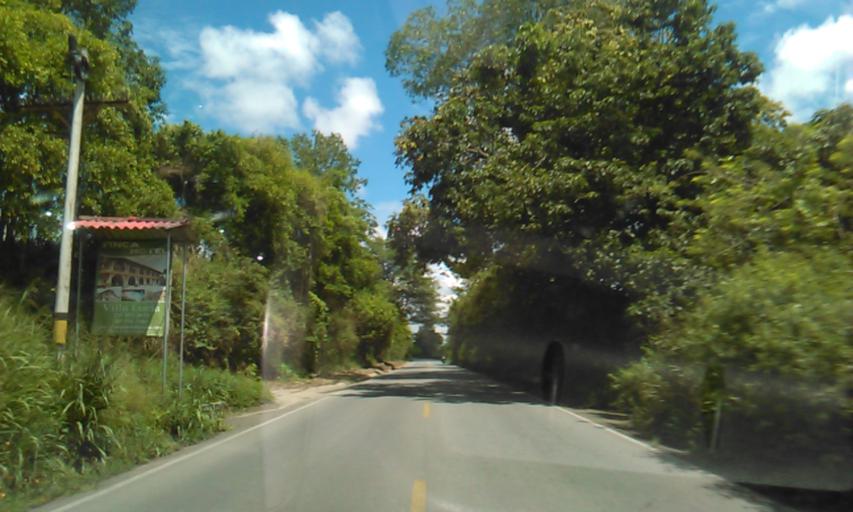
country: CO
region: Quindio
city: Cordoba
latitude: 4.4150
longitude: -75.7252
